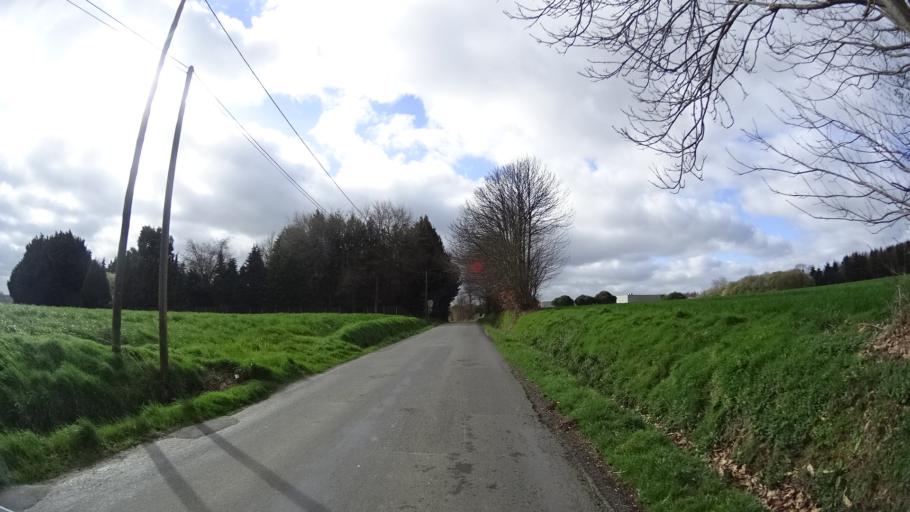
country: FR
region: Brittany
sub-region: Departement d'Ille-et-Vilaine
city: La Meziere
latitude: 48.2081
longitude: -1.7309
